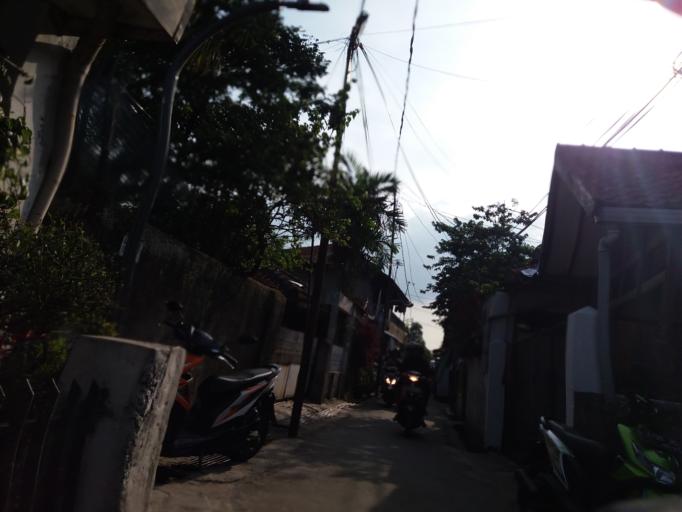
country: ID
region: West Java
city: Bandung
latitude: -6.9543
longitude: 107.6376
